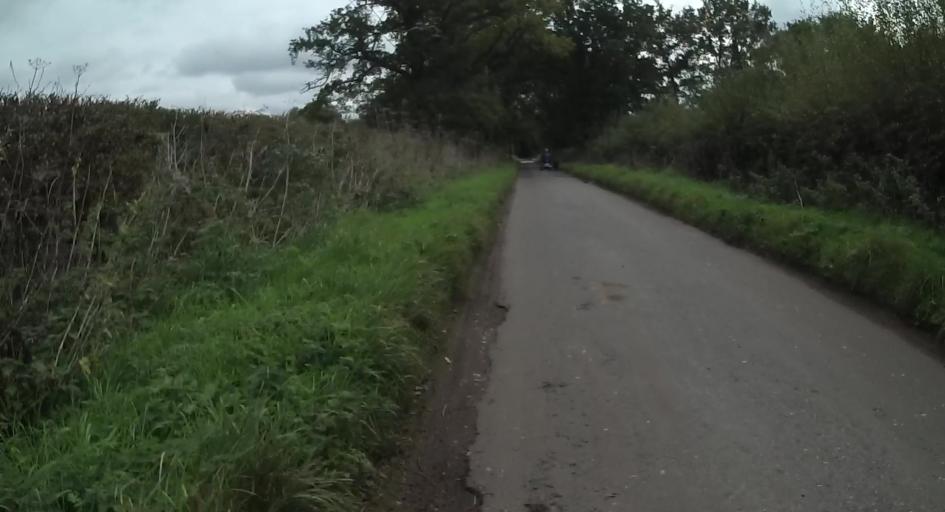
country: GB
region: England
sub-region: Hampshire
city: Eversley
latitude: 51.3631
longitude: -0.9061
